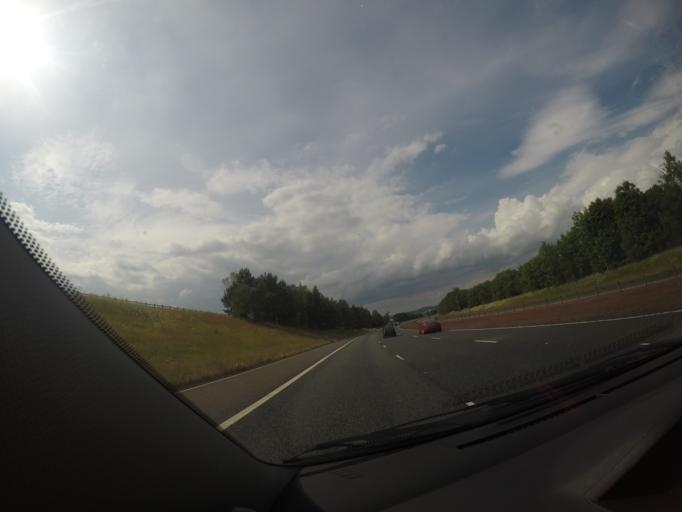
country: GB
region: Scotland
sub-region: Dumfries and Galloway
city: Lochmaben
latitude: 55.1762
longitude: -3.4017
